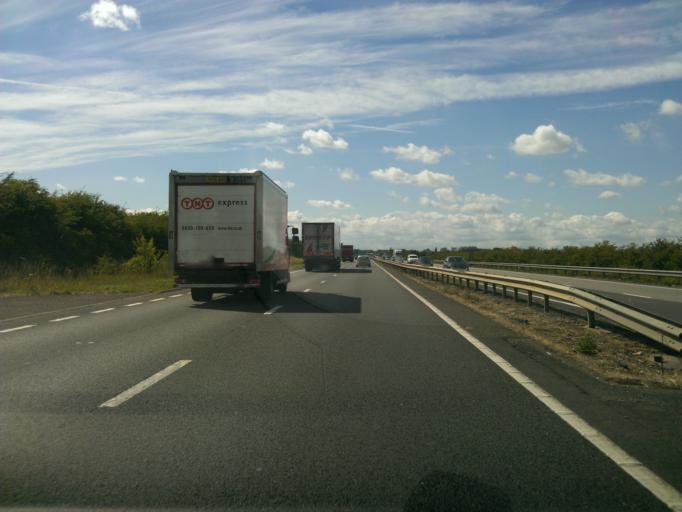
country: GB
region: England
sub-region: Bedford
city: Pertenhall
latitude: 52.3619
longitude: -0.4152
